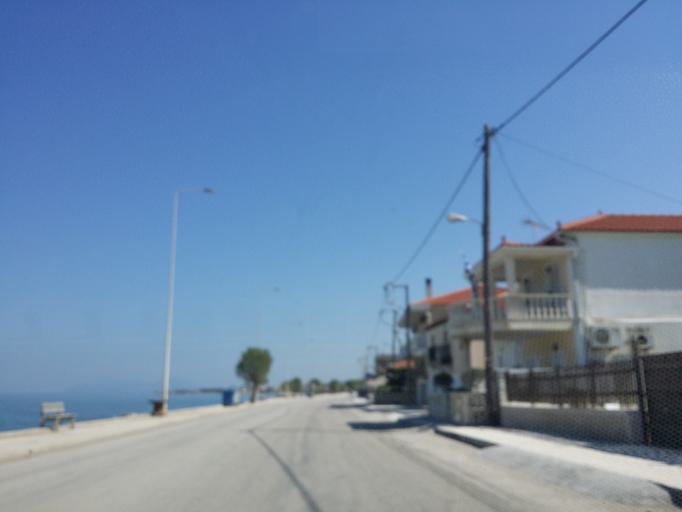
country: GR
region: Peloponnese
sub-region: Nomos Korinthias
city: Xylokastro
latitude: 38.1081
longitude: 22.5381
